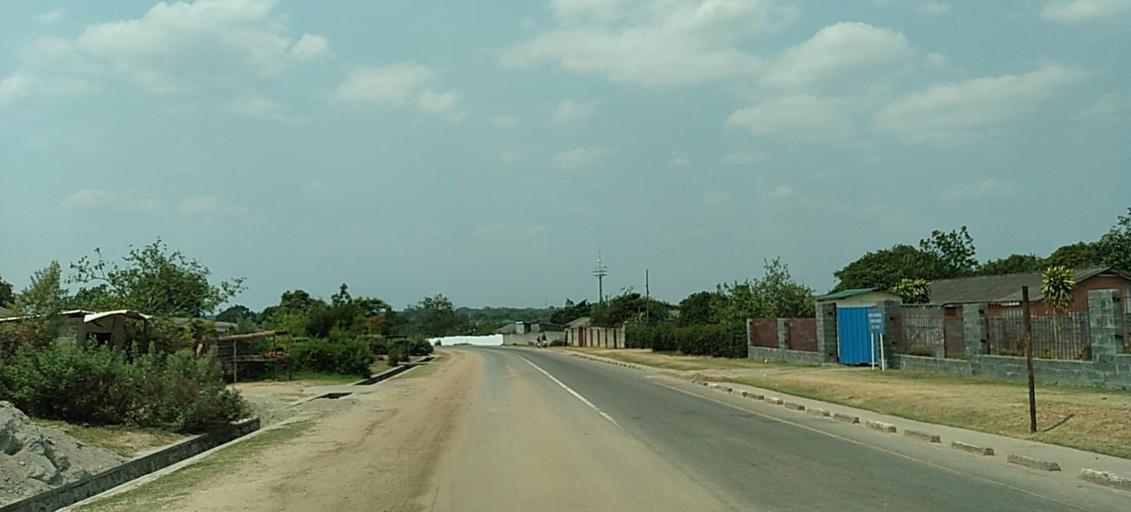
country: ZM
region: Copperbelt
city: Chambishi
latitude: -12.6339
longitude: 28.0582
